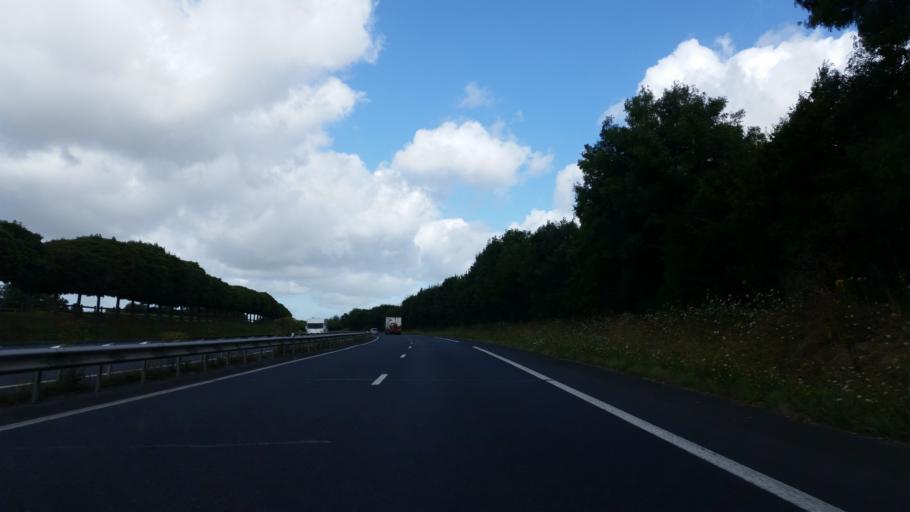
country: FR
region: Lower Normandy
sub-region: Departement du Calvados
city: Grandcamp-Maisy
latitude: 49.3413
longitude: -1.0168
